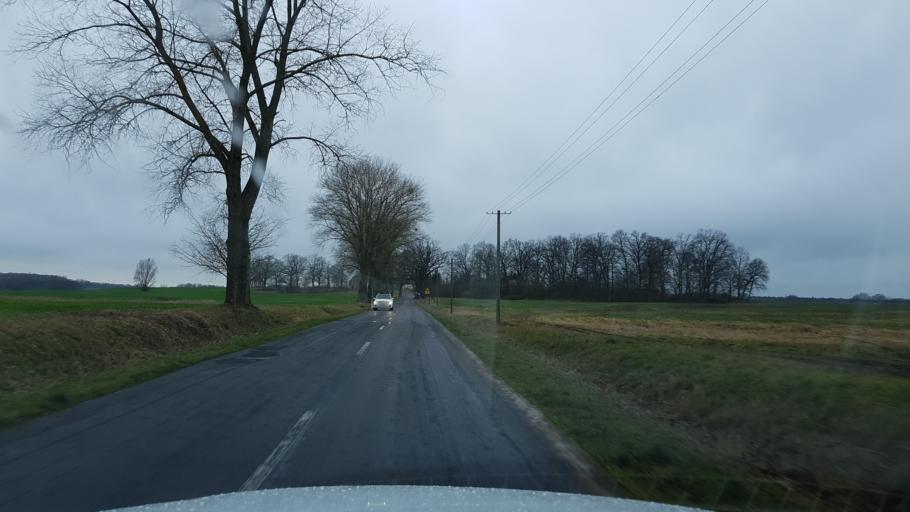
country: PL
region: West Pomeranian Voivodeship
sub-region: Powiat lobeski
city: Radowo Male
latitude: 53.6127
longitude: 15.4649
